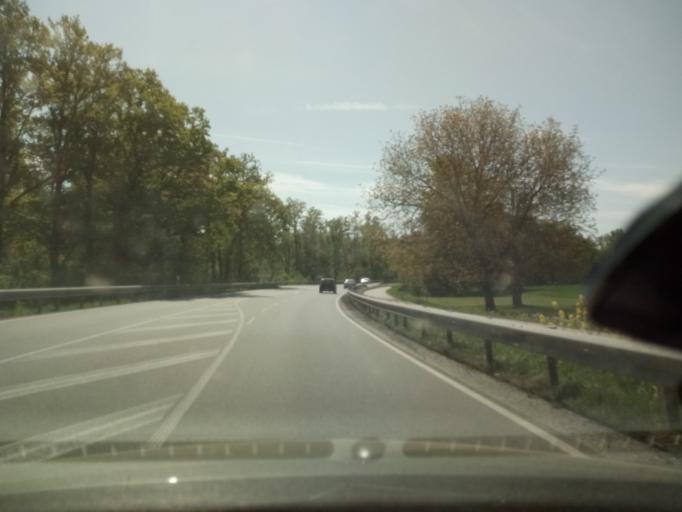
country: DE
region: Bavaria
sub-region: Upper Bavaria
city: Ampfing
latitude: 48.2335
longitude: 12.4141
